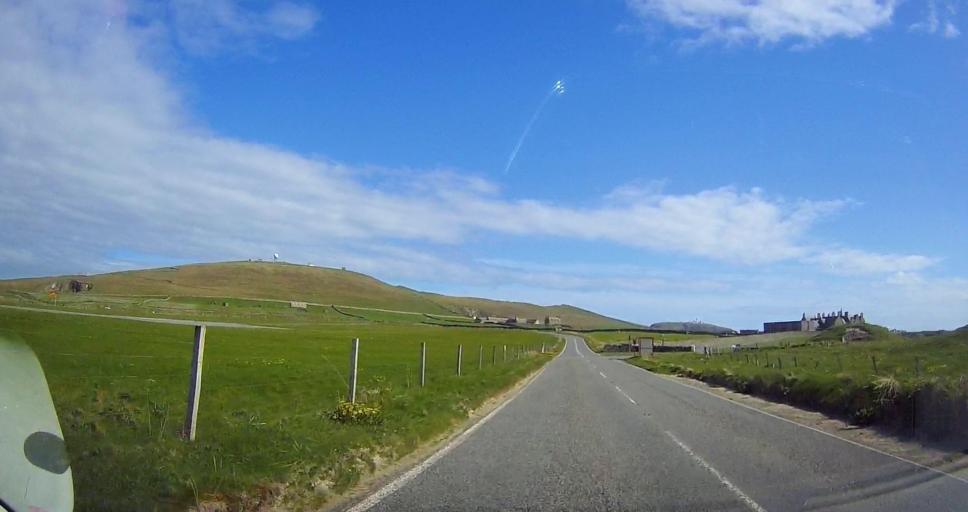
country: GB
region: Scotland
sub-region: Shetland Islands
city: Sandwick
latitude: 59.8726
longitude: -1.2884
